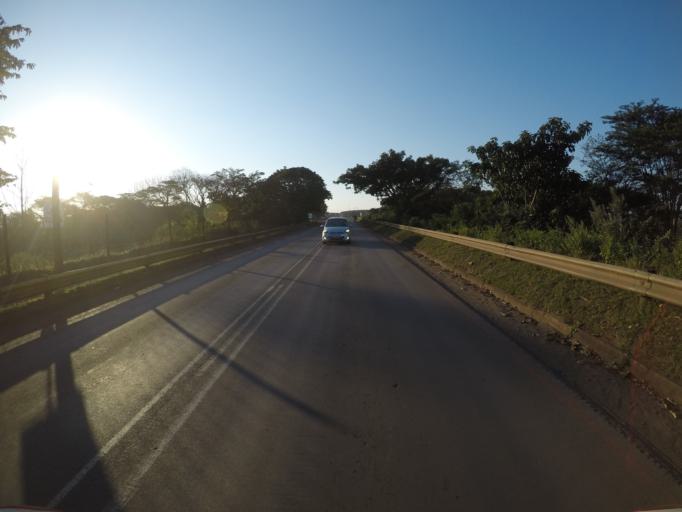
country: ZA
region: KwaZulu-Natal
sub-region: uThungulu District Municipality
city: KwaMbonambi
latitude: -28.6852
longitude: 32.1423
